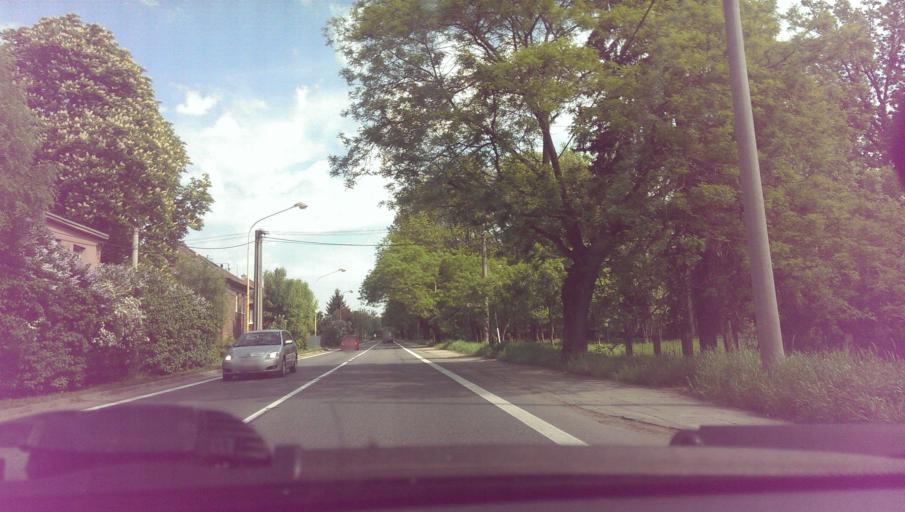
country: CZ
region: Zlin
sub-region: Okres Zlin
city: Napajedla
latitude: 49.1659
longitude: 17.5053
